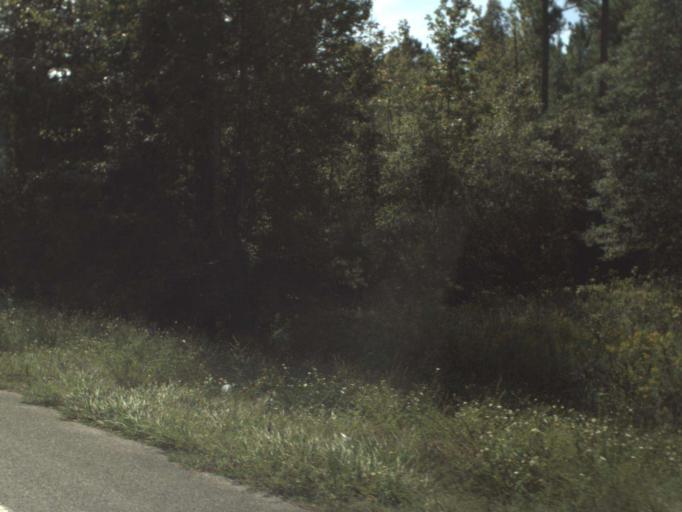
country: US
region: Florida
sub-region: Washington County
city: Chipley
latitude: 30.6090
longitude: -85.5938
